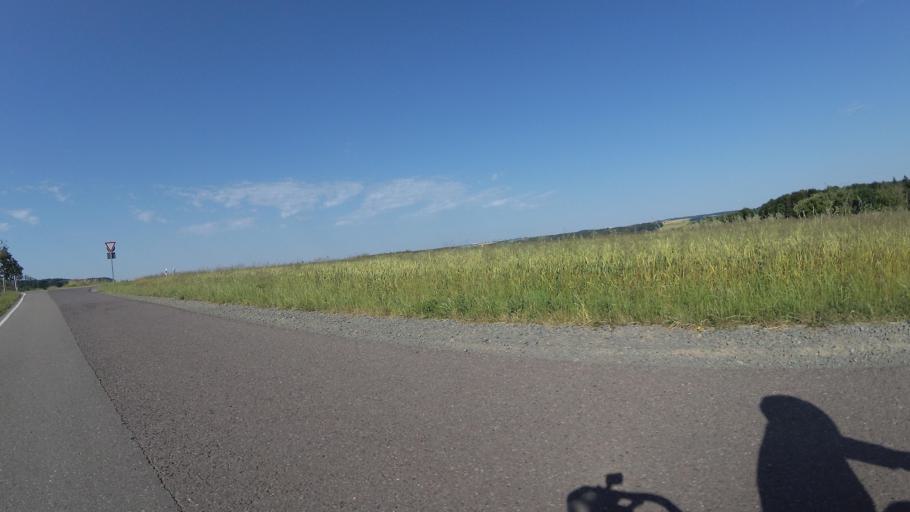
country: DE
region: Rheinland-Pfalz
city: Althornbach
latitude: 49.2173
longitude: 7.3238
